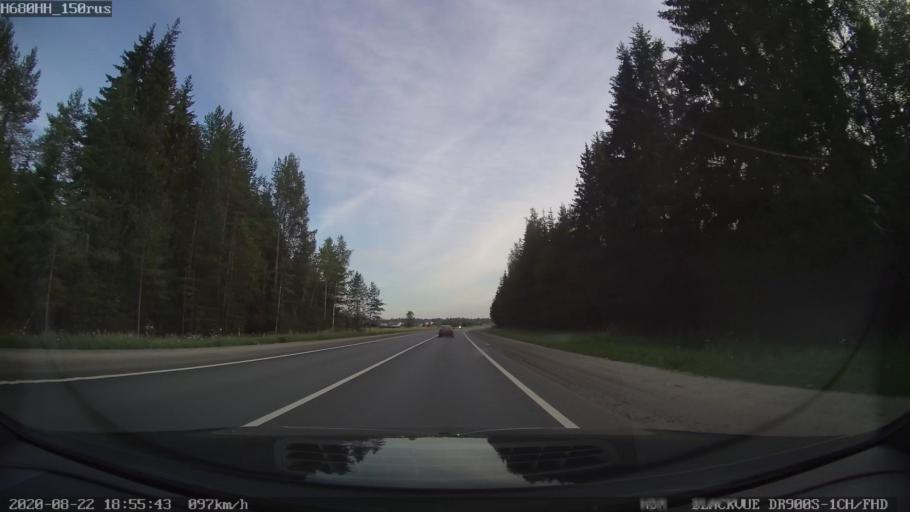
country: RU
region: Tverskaya
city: Rameshki
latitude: 57.1946
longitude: 36.0836
